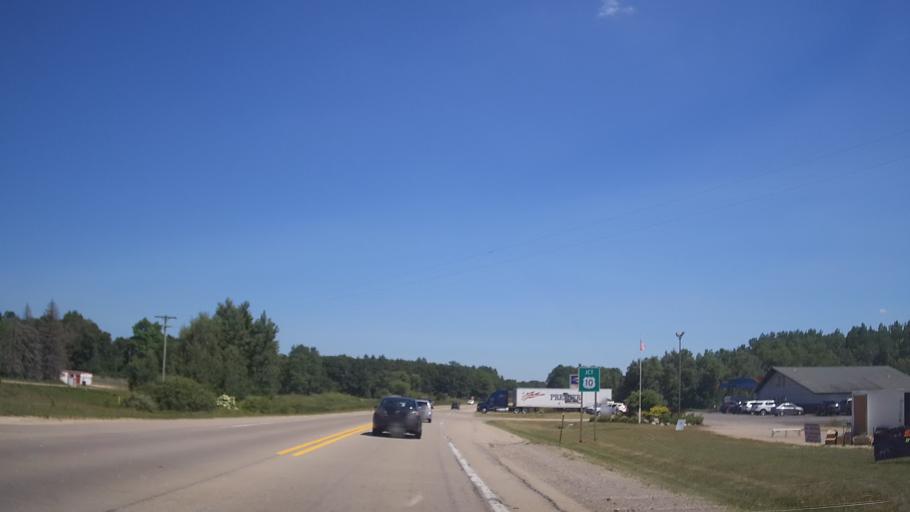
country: US
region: Michigan
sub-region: Clare County
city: Clare
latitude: 43.8683
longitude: -84.9167
